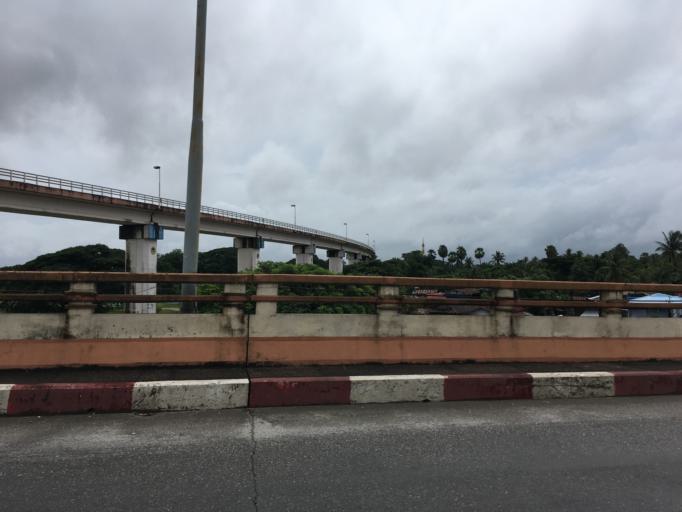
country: MM
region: Mon
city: Martaban
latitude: 16.5240
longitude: 97.6108
